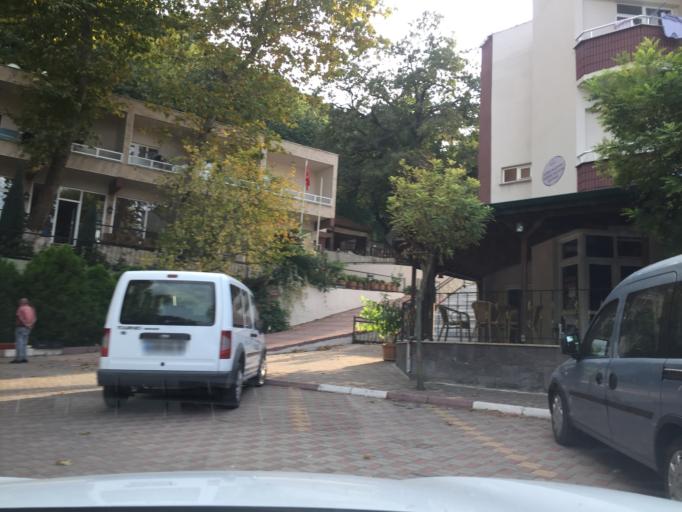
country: TR
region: Balikesir
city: Gonen
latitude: 40.0299
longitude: 27.5626
